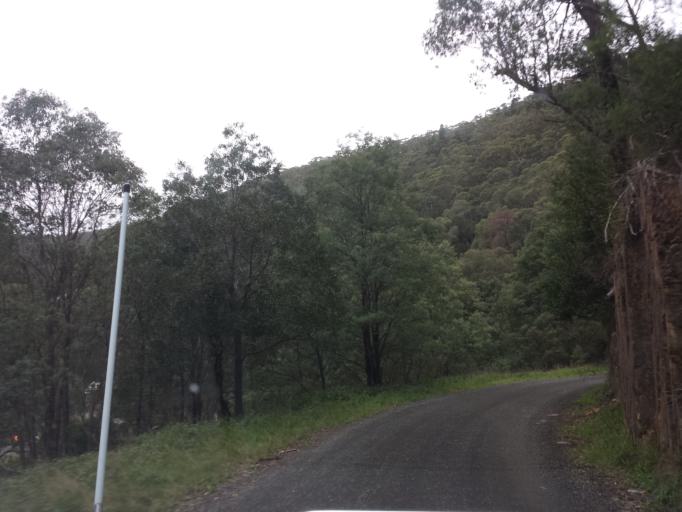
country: AU
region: Victoria
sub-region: Latrobe
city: Traralgon
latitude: -37.9509
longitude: 146.4486
